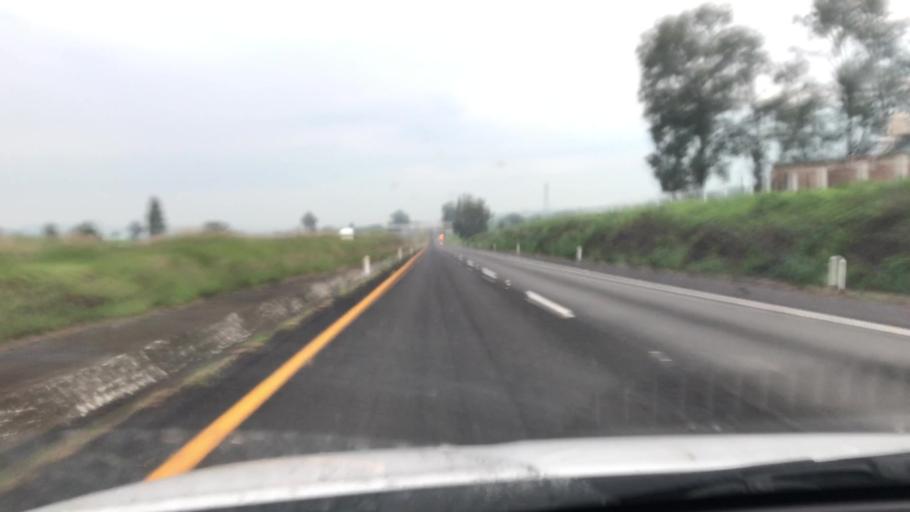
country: MX
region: Jalisco
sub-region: Zapotlanejo
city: La Mezquitera
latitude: 20.5596
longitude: -103.0704
